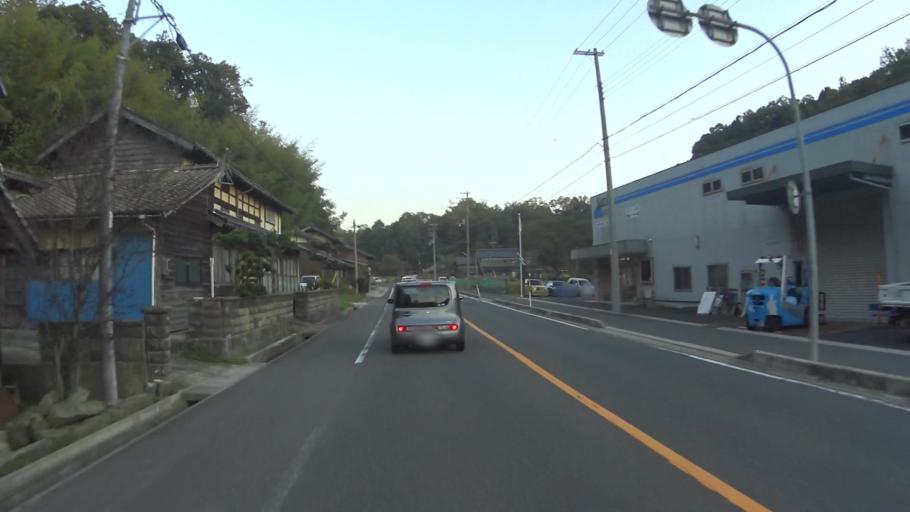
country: JP
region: Kyoto
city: Miyazu
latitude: 35.6474
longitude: 135.0439
